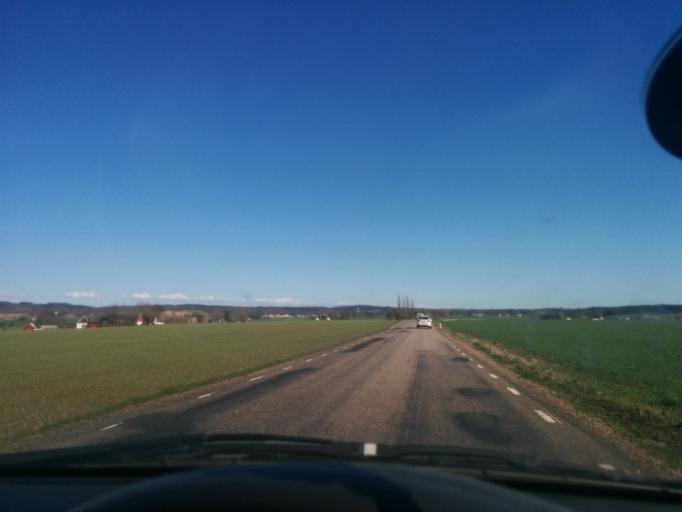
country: SE
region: Skane
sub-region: Lunds Kommun
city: Genarp
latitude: 55.6109
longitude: 13.3573
